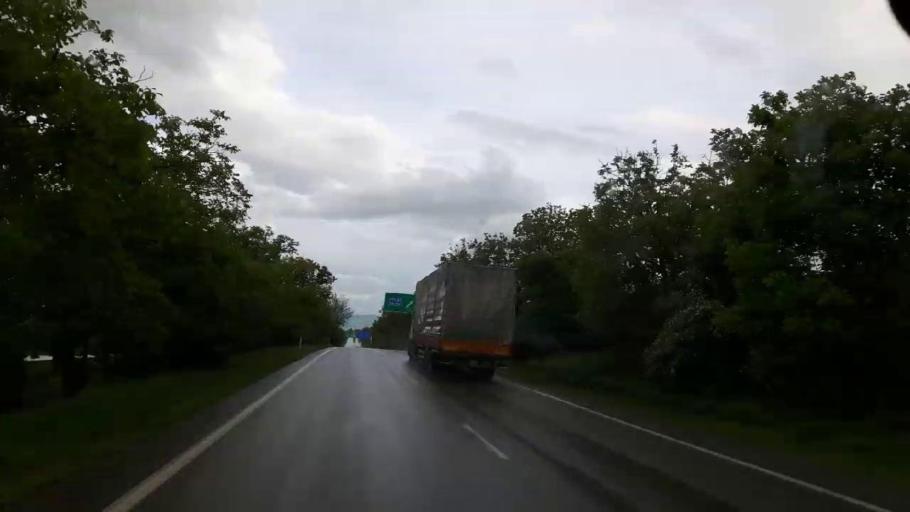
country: GE
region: Shida Kartli
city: Kaspi
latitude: 41.9668
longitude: 44.4631
